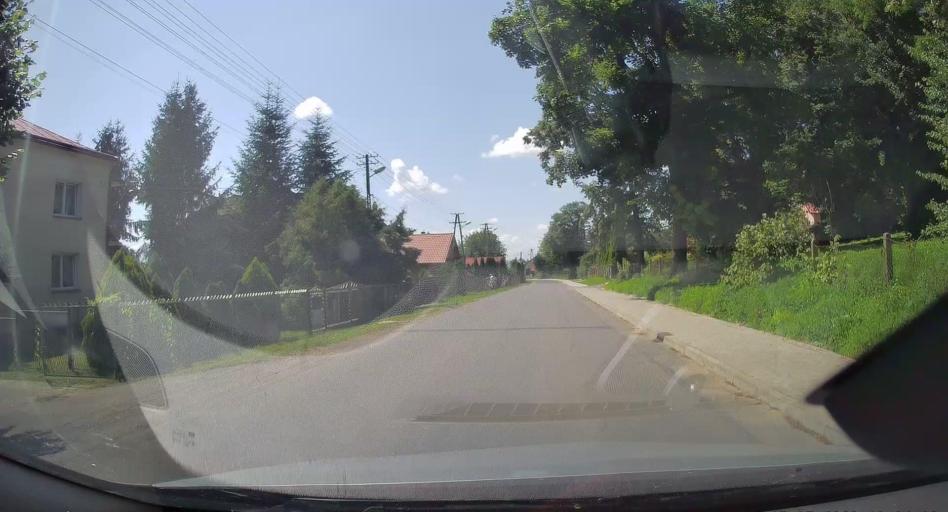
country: PL
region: Subcarpathian Voivodeship
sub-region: Powiat przemyski
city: Medyka
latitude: 49.8384
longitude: 22.8833
